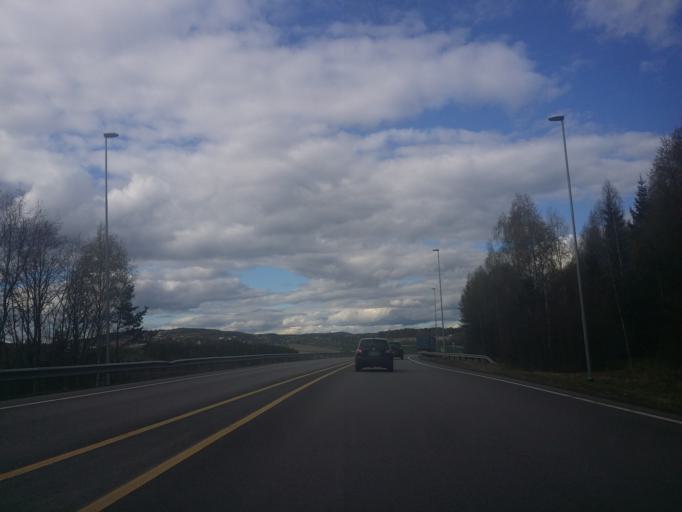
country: NO
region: Buskerud
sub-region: Ringerike
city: Honefoss
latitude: 60.1547
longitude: 10.2186
